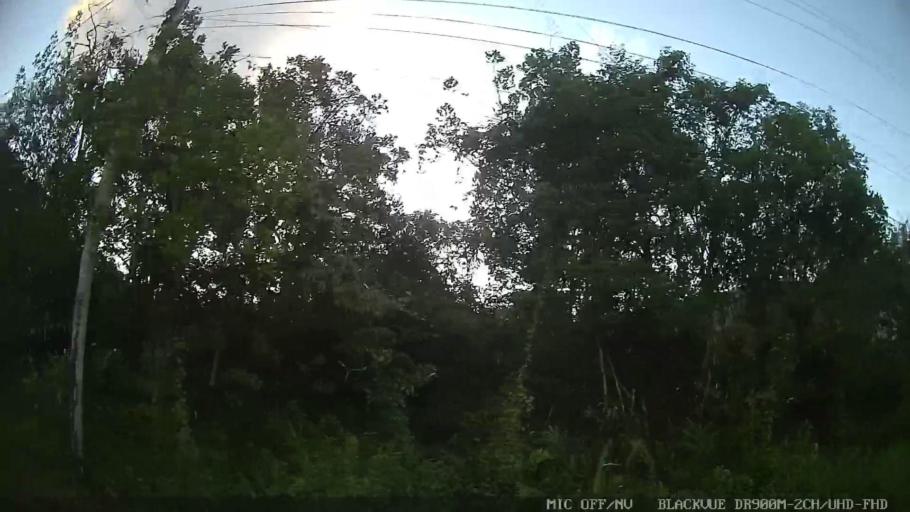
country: BR
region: Sao Paulo
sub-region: Itanhaem
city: Itanhaem
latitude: -24.1455
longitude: -46.7368
